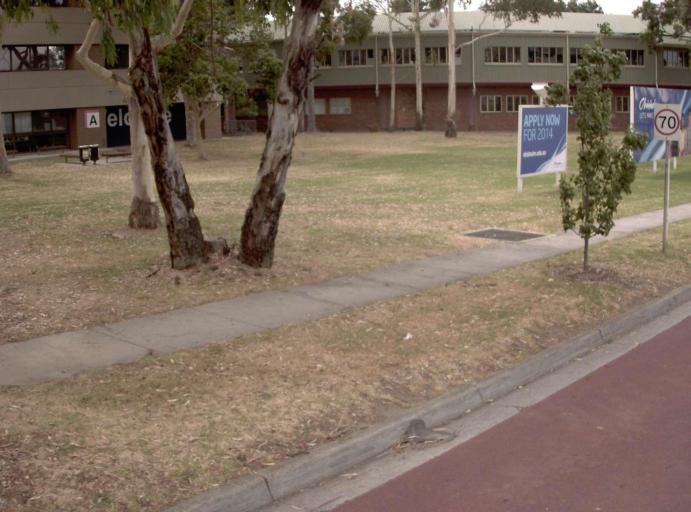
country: AU
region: Victoria
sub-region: Greater Dandenong
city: Dandenong North
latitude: -37.9758
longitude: 145.2225
